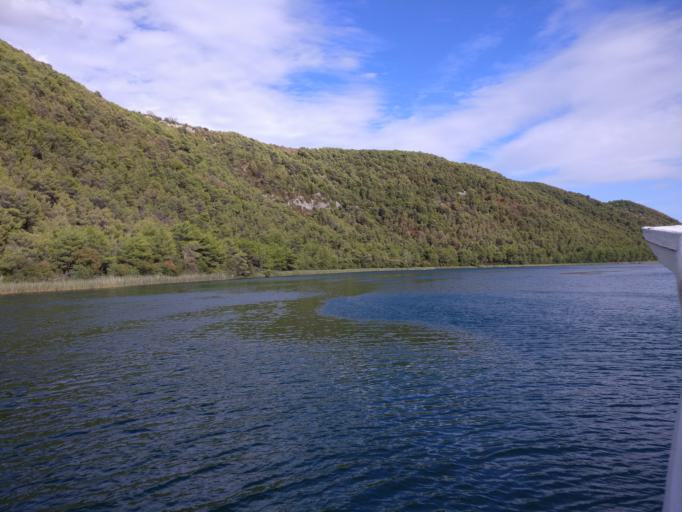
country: HR
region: Sibensko-Kniniska
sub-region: Grad Sibenik
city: Sibenik
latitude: 43.8217
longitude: 15.9429
